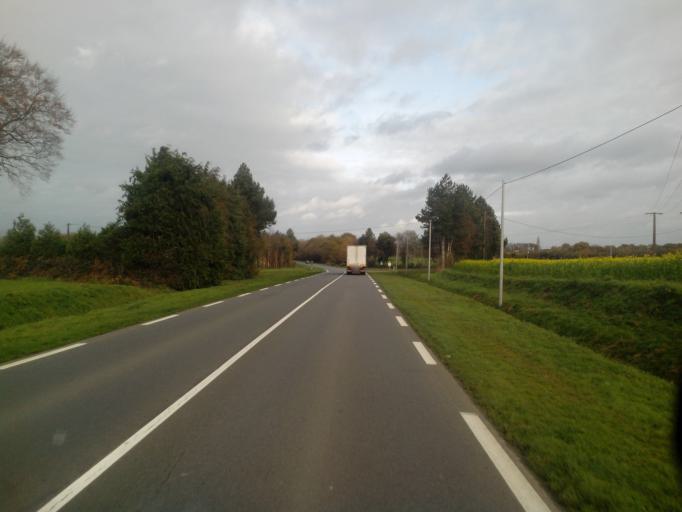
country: FR
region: Brittany
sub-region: Departement d'Ille-et-Vilaine
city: Gael
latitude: 48.1521
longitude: -2.2139
